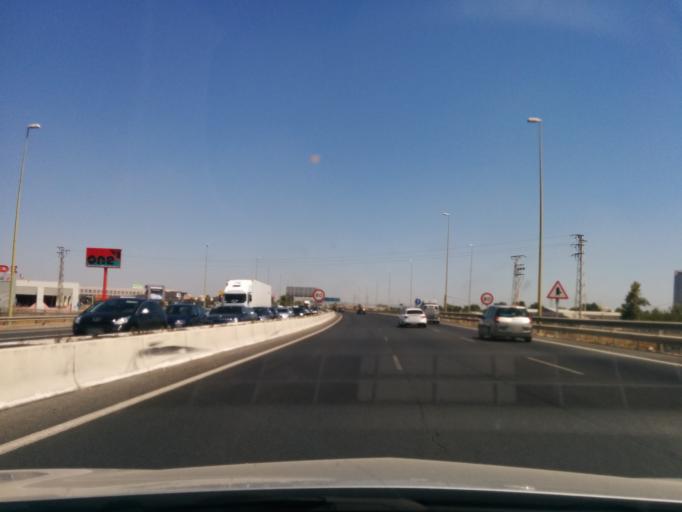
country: ES
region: Andalusia
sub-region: Provincia de Sevilla
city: Tomares
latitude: 37.3751
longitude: -6.0270
